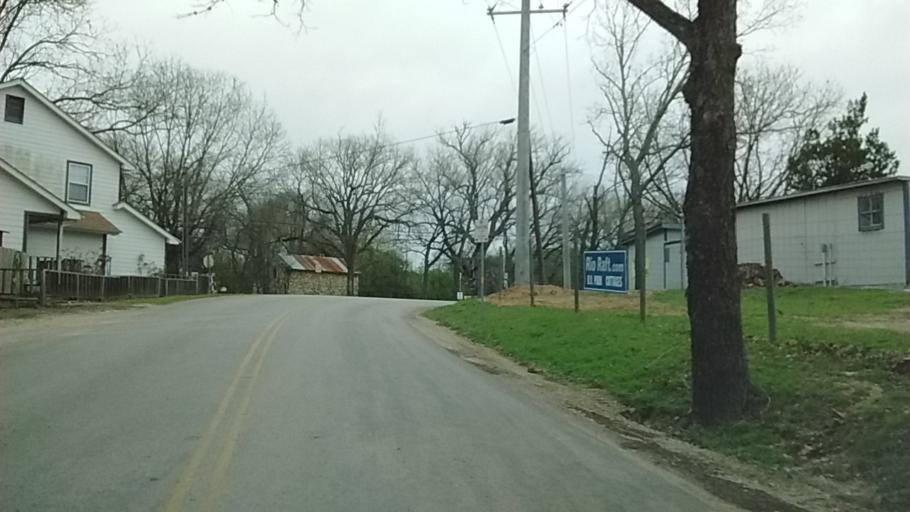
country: US
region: Texas
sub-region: Comal County
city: Canyon Lake
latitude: 29.8432
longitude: -98.1687
